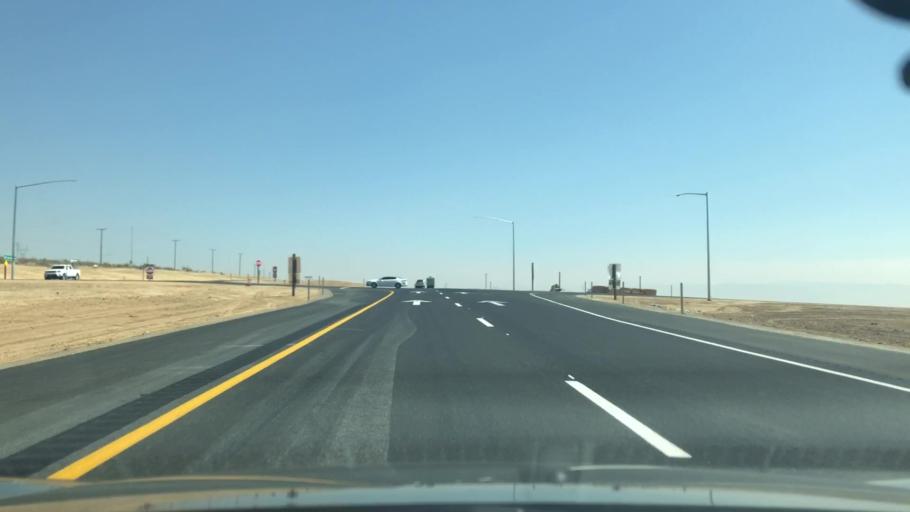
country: US
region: California
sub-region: Kern County
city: Inyokern
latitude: 35.6401
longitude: -117.8828
